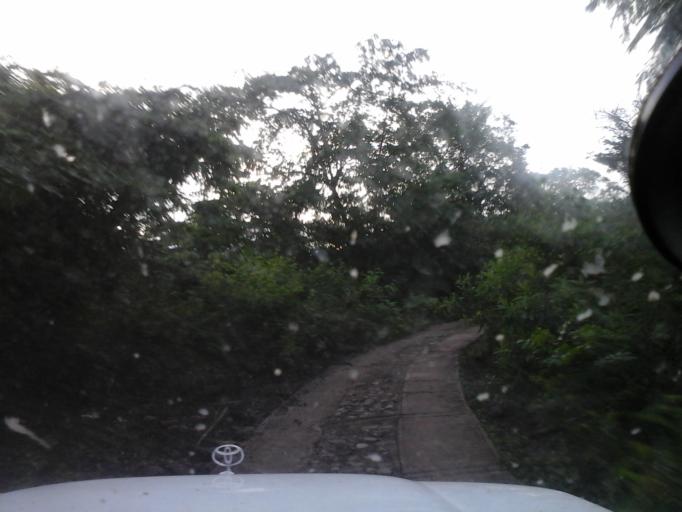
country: CO
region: Cesar
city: Agustin Codazzi
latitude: 10.1737
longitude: -73.1519
